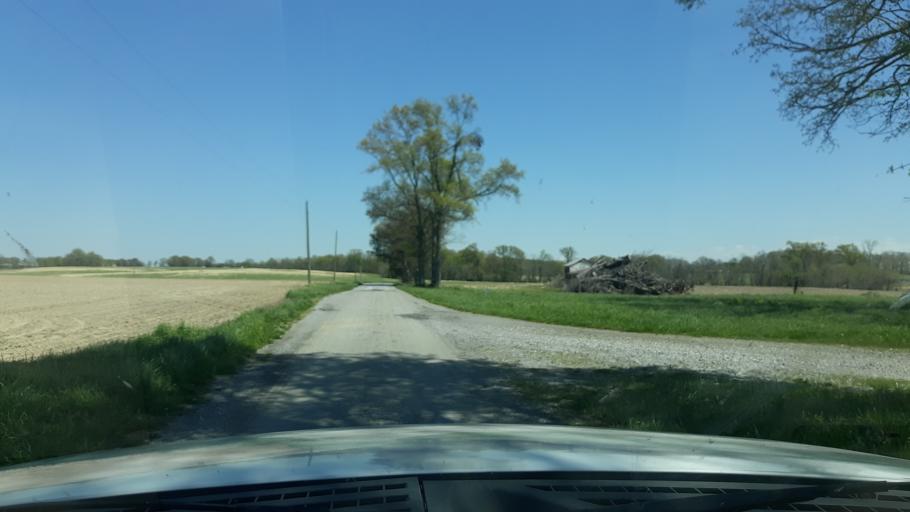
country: US
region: Illinois
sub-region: Saline County
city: Harrisburg
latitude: 37.8887
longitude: -88.6738
